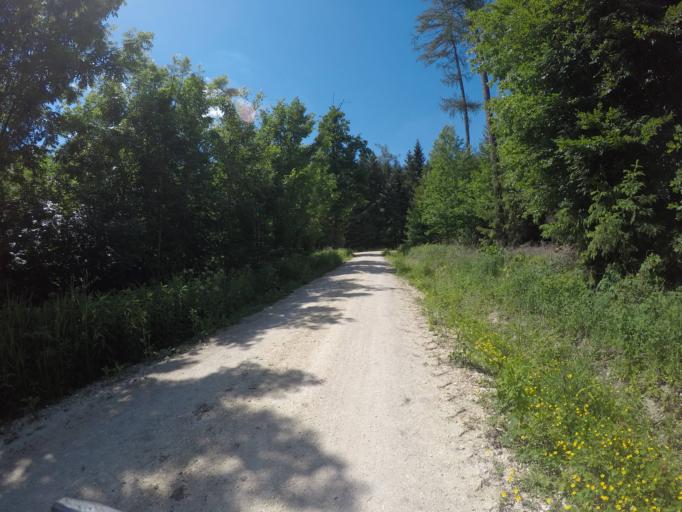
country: DE
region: Bavaria
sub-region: Lower Bavaria
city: Kumhausen
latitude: 48.5056
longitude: 12.1937
